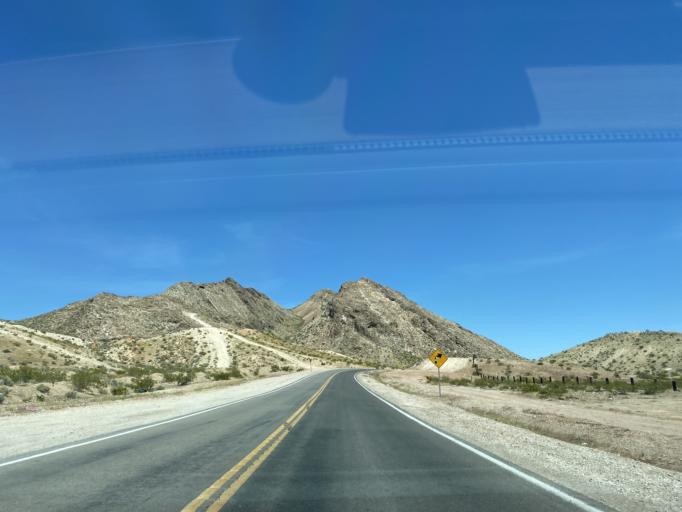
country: US
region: Nevada
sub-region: Clark County
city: Nellis Air Force Base
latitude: 36.2024
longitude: -114.9893
